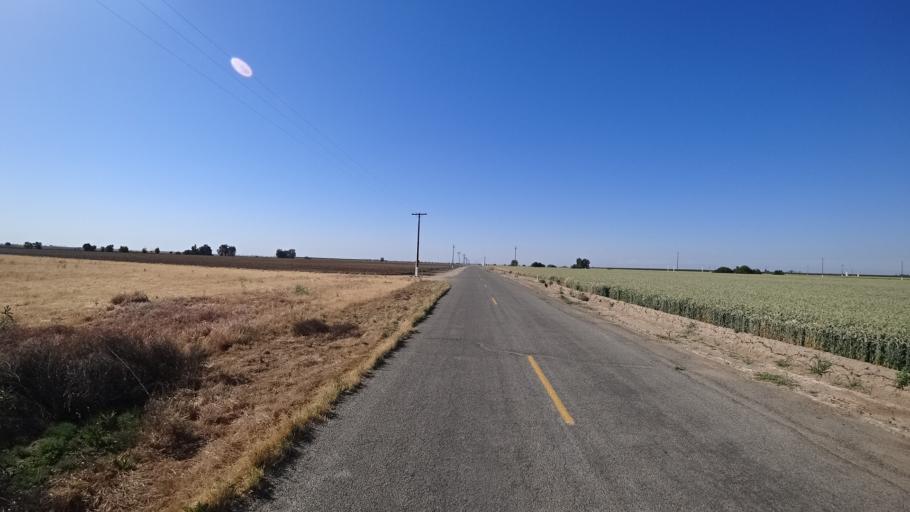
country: US
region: California
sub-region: Kings County
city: Home Garden
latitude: 36.2235
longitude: -119.5651
